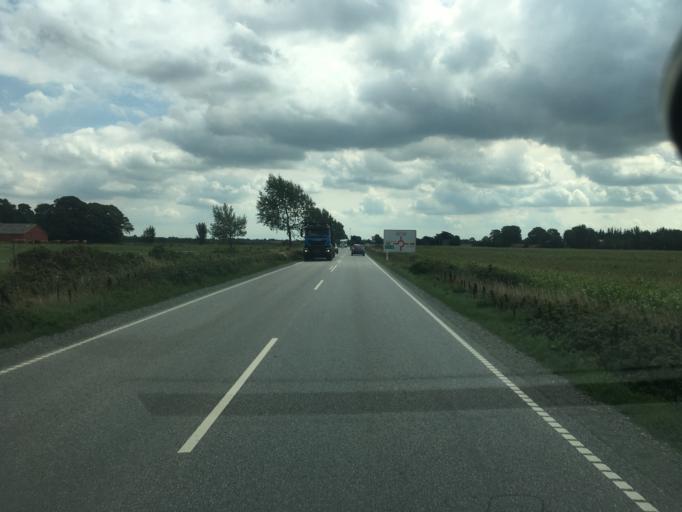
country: DK
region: South Denmark
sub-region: Aabenraa Kommune
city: Tinglev
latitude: 54.9726
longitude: 9.3077
